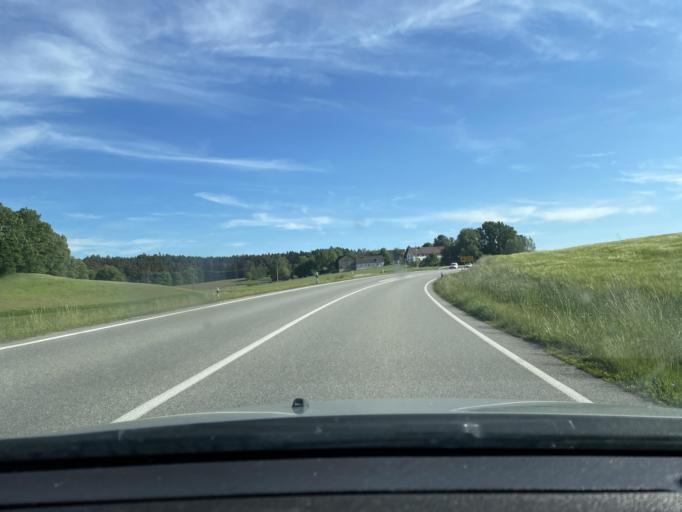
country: DE
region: Bavaria
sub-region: Lower Bavaria
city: Pfeffenhausen
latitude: 48.6472
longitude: 11.9762
